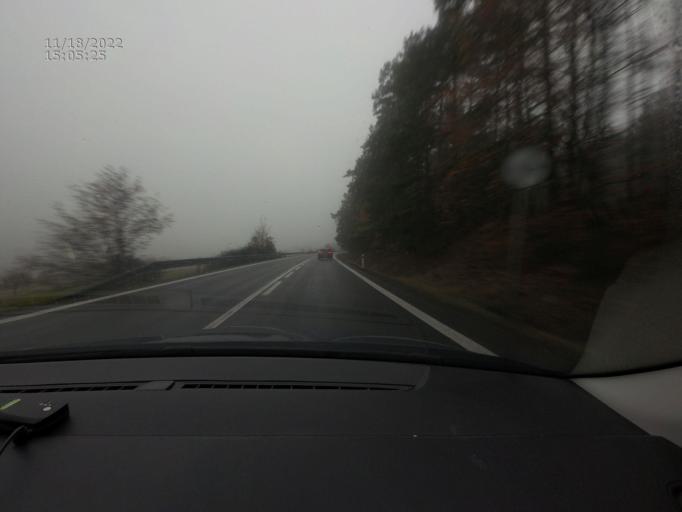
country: CZ
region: Jihocesky
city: Cimelice
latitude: 49.5004
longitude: 14.1367
